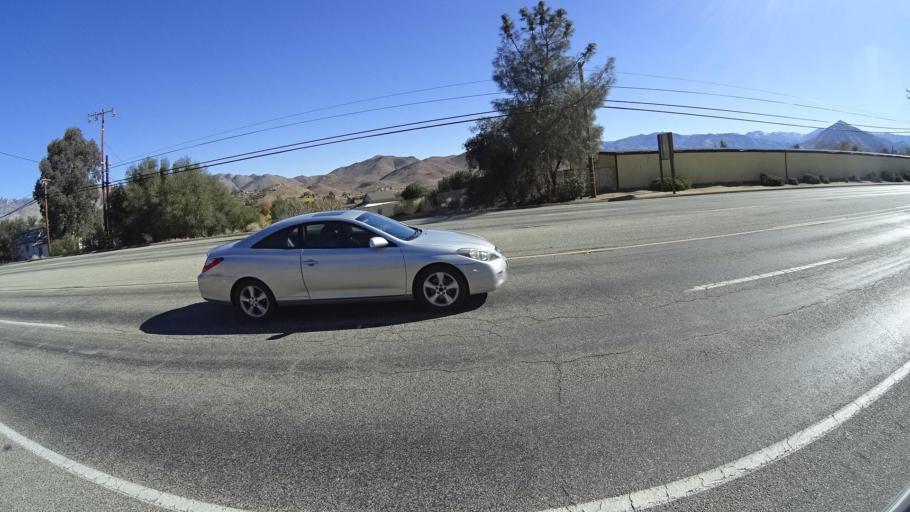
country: US
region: California
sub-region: Kern County
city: Wofford Heights
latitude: 35.7058
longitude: -118.4572
